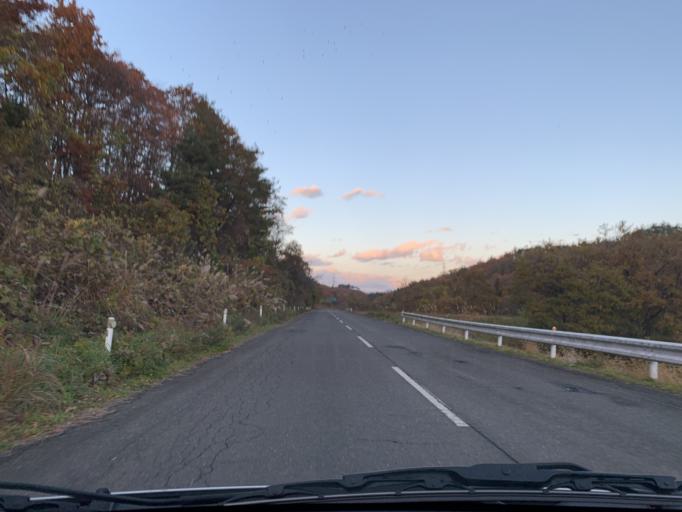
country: JP
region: Iwate
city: Ichinoseki
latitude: 39.0042
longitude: 141.0481
